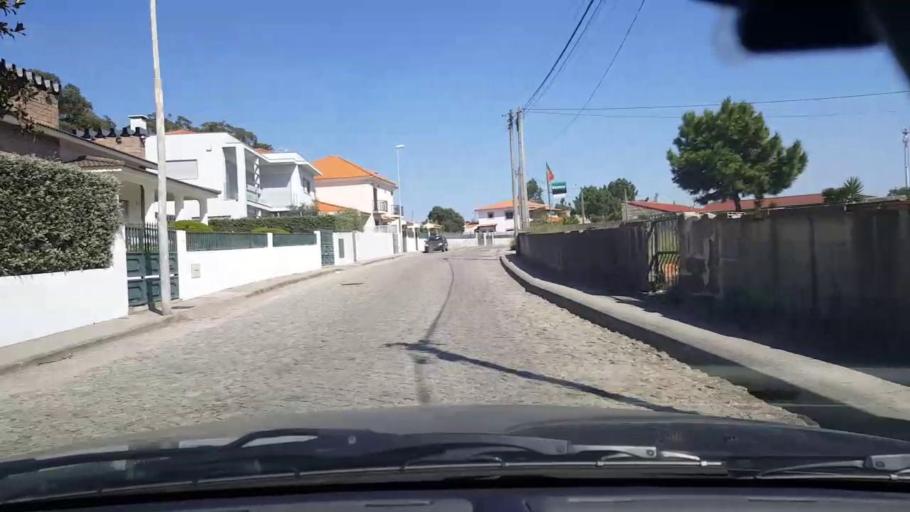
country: PT
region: Porto
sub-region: Matosinhos
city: Lavra
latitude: 41.2978
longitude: -8.7295
